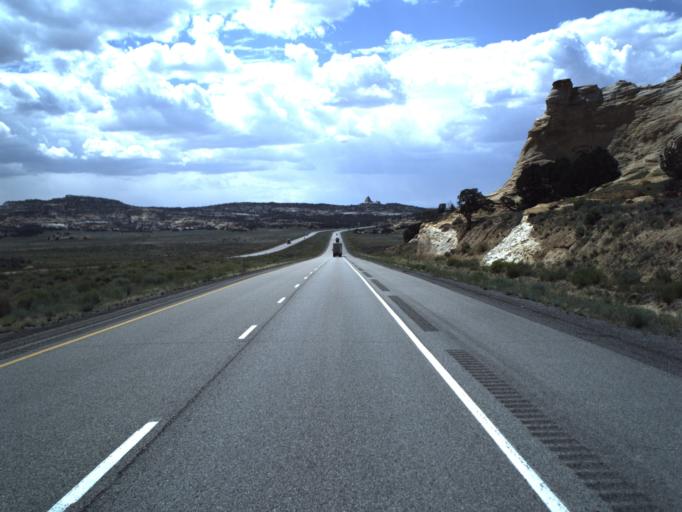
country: US
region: Utah
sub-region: Emery County
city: Castle Dale
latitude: 38.8695
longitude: -110.7743
